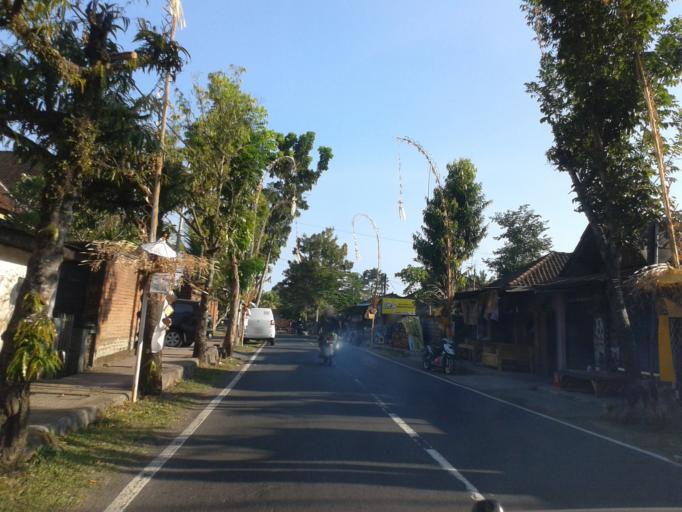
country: ID
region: Bali
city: Banjar Wangsian
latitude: -8.4933
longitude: 115.4027
